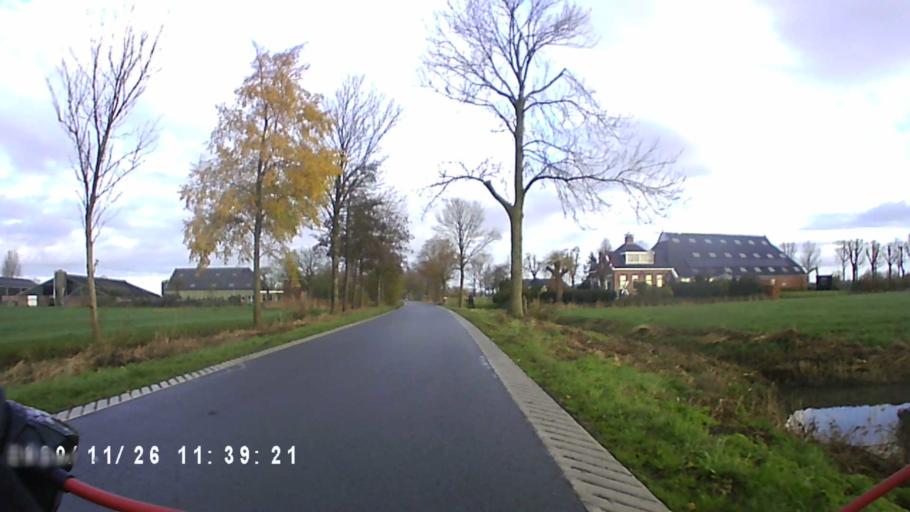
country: NL
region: Groningen
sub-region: Gemeente Bedum
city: Bedum
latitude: 53.2839
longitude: 6.5692
